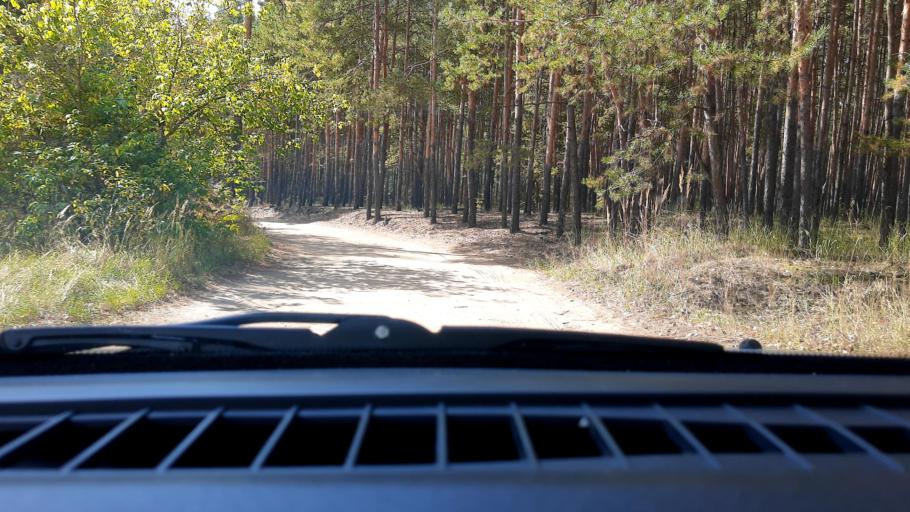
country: RU
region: Nizjnij Novgorod
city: Gorbatovka
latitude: 56.3111
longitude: 43.6989
